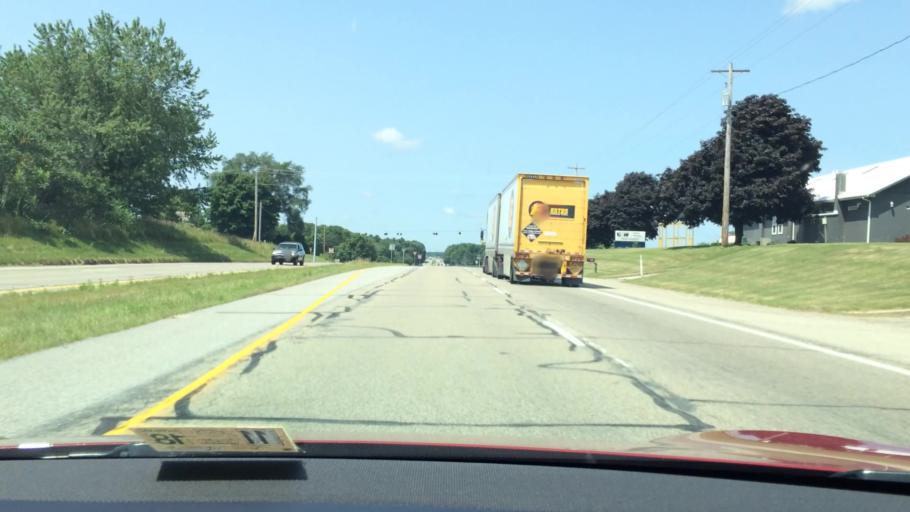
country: US
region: Indiana
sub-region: LaPorte County
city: Hudson Lake
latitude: 41.6727
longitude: -86.5632
